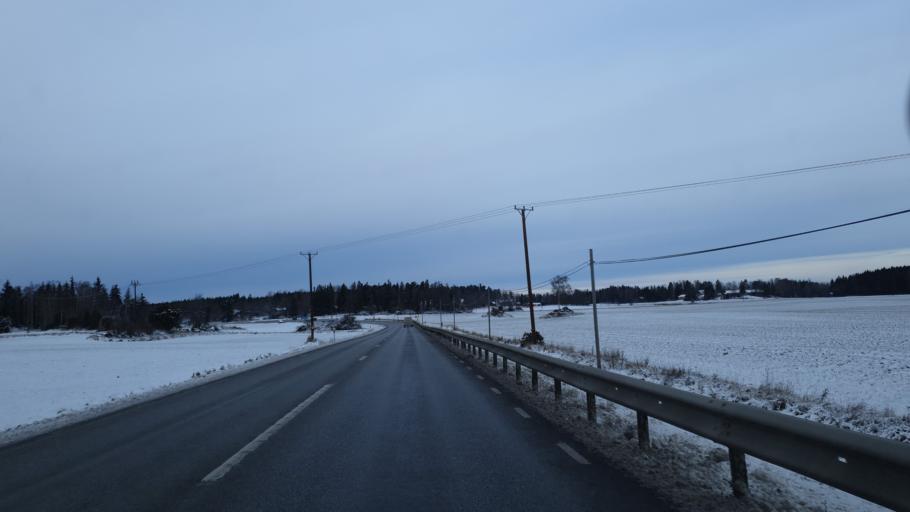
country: SE
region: Uppsala
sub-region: Habo Kommun
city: Balsta
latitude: 59.6280
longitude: 17.6016
